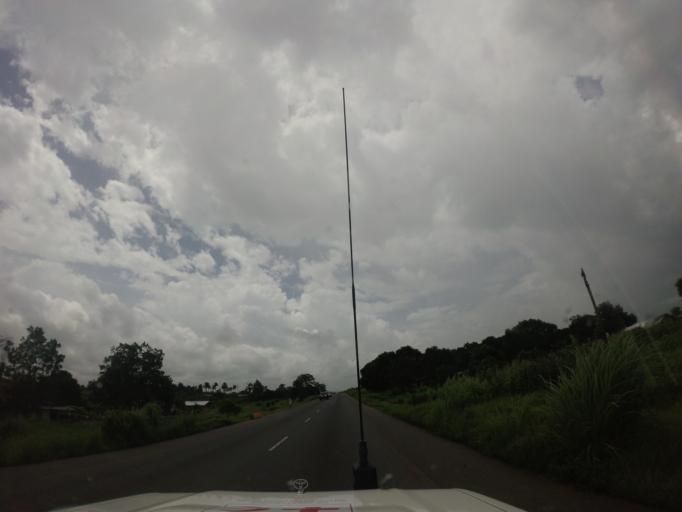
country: SL
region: Western Area
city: Waterloo
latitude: 8.4237
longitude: -12.8919
